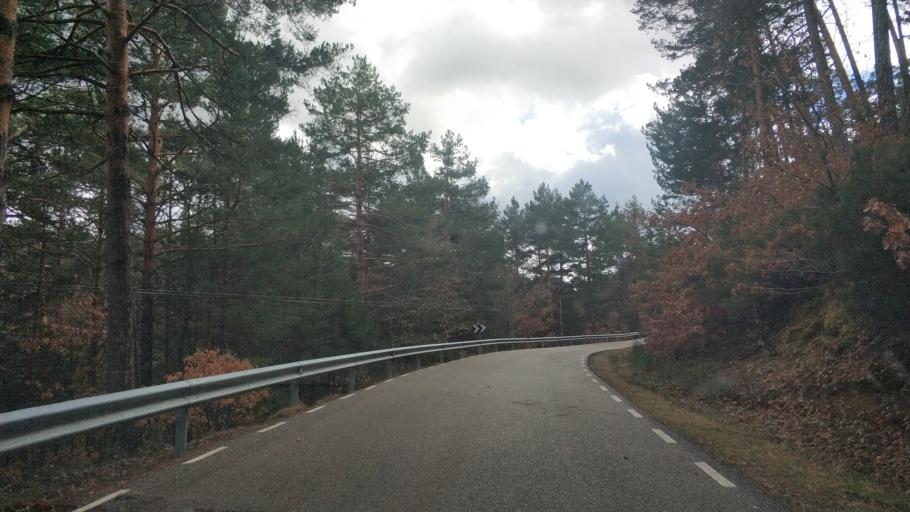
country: ES
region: Castille and Leon
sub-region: Provincia de Burgos
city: Quintanar de la Sierra
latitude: 42.0036
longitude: -3.0185
